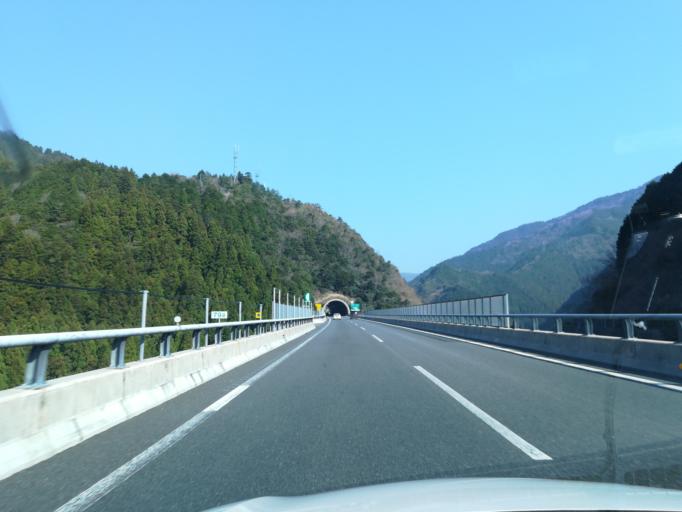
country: JP
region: Ehime
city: Kawanoecho
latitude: 33.8240
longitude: 133.6622
